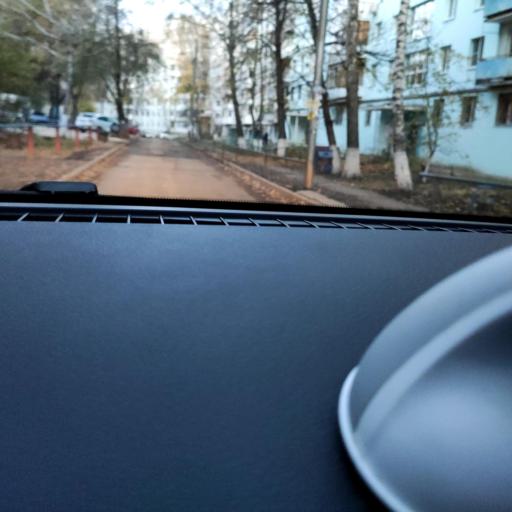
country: RU
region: Samara
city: Samara
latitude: 53.2441
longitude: 50.2573
